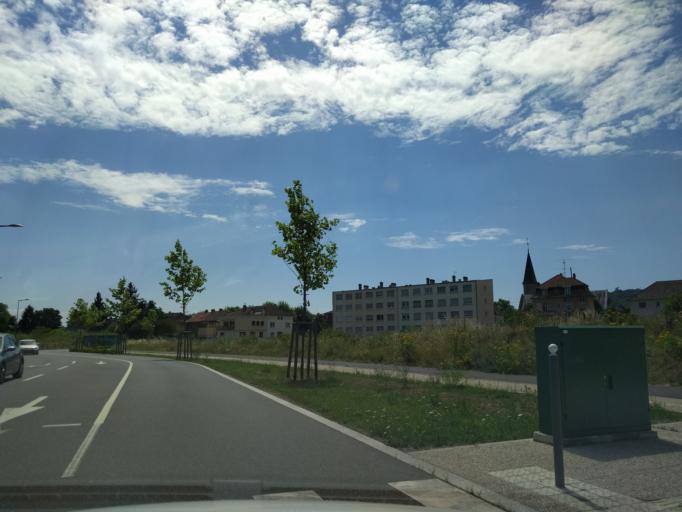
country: FR
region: Lorraine
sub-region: Departement de la Moselle
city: Le Ban Saint-Martin
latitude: 49.1359
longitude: 6.1581
